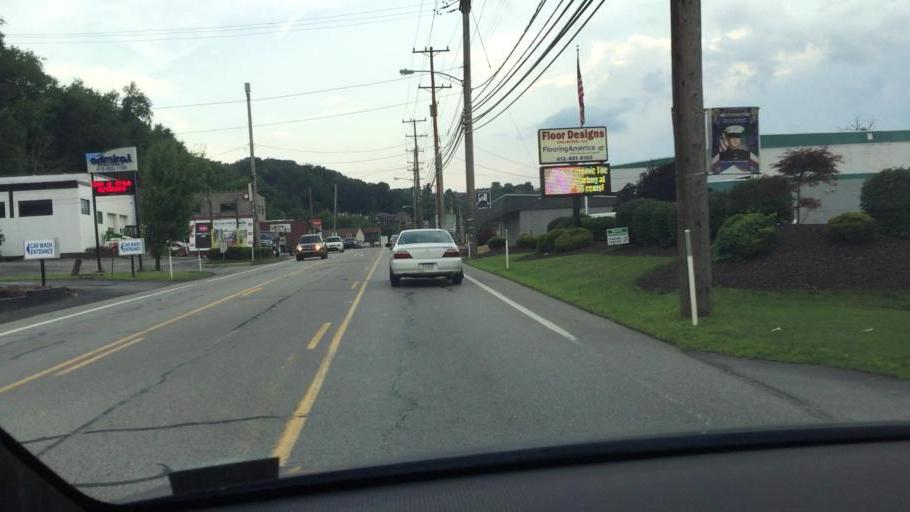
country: US
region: Pennsylvania
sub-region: Allegheny County
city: Castle Shannon
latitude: 40.3694
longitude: -80.0114
